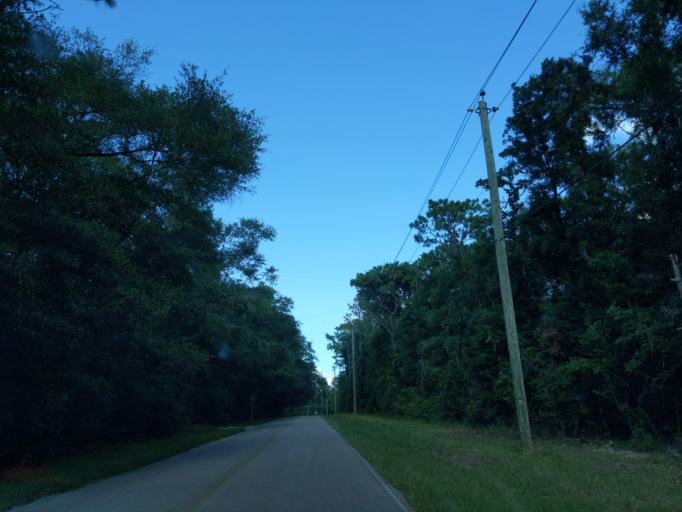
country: US
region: Florida
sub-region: Leon County
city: Tallahassee
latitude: 30.3995
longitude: -84.3385
